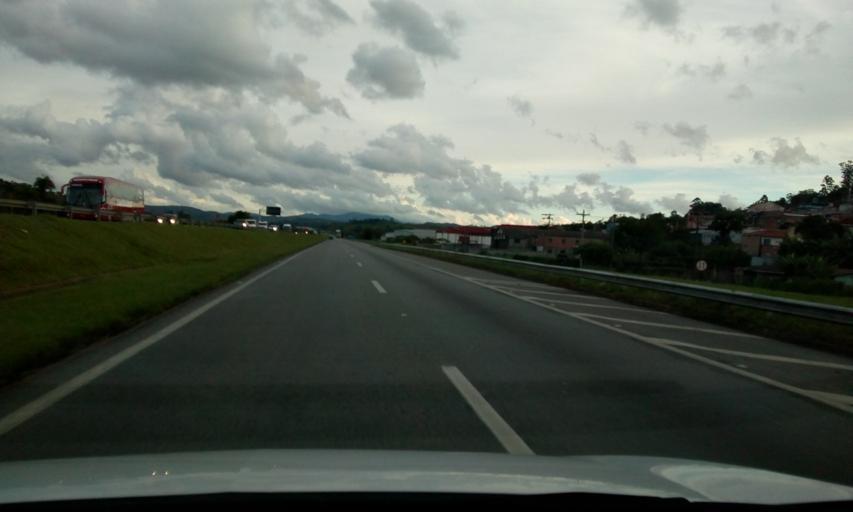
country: BR
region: Sao Paulo
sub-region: Bom Jesus Dos Perdoes
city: Bom Jesus dos Perdoes
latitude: -23.1357
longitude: -46.4601
